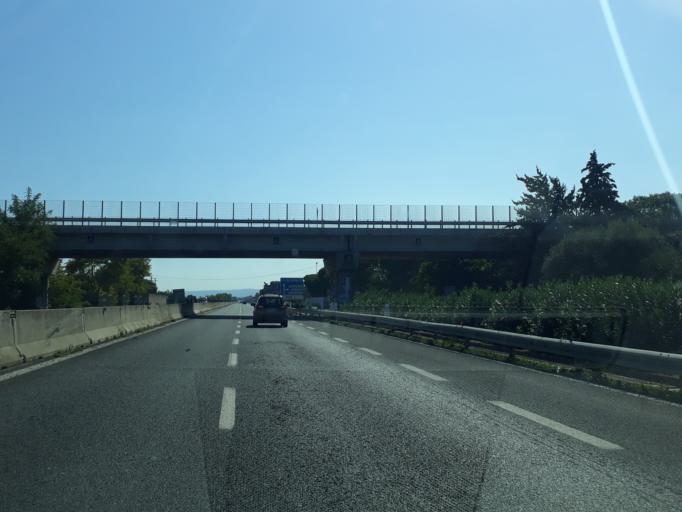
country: IT
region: Apulia
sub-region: Provincia di Bari
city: Monopoli
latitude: 40.9072
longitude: 17.3241
